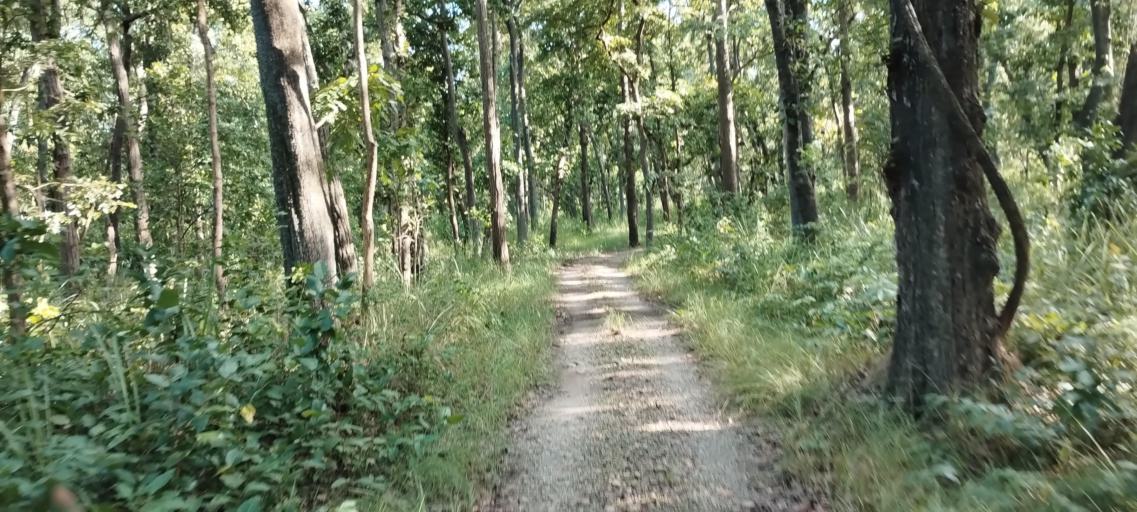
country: NP
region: Far Western
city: Tikapur
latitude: 28.5303
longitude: 81.2830
